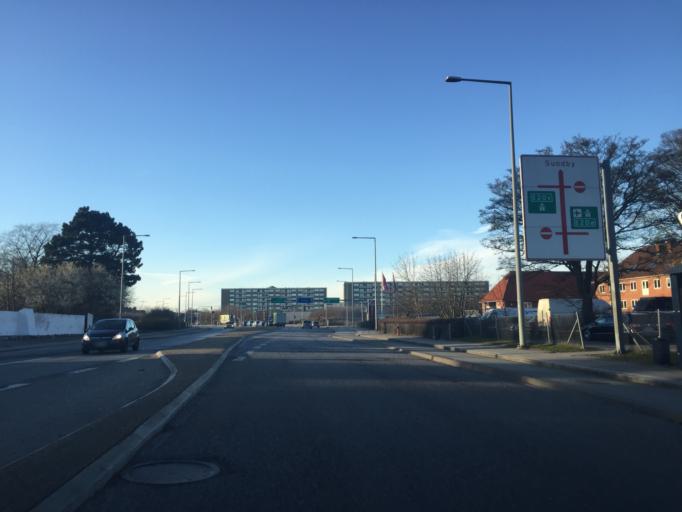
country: DK
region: Capital Region
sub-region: Tarnby Kommune
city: Tarnby
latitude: 55.6277
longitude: 12.6040
